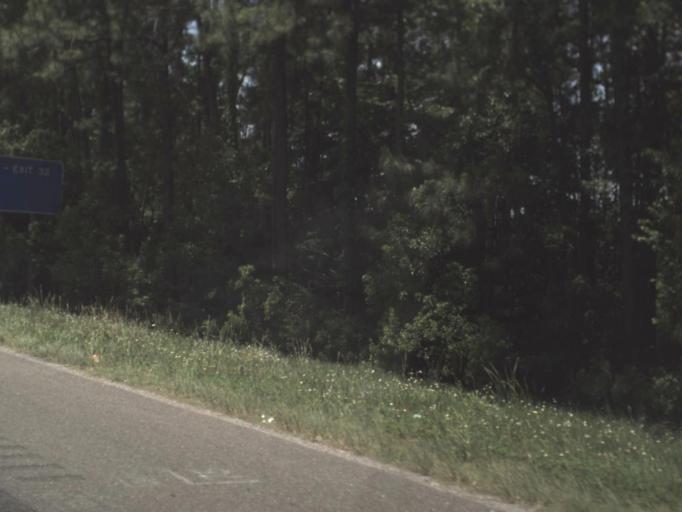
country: US
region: Florida
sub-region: Nassau County
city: Nassau Village-Ratliff
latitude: 30.4587
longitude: -81.6959
